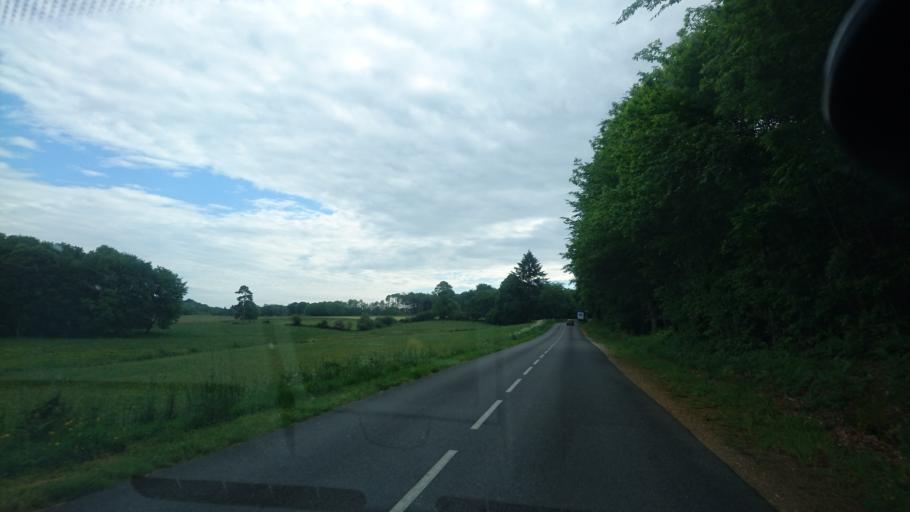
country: FR
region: Limousin
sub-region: Departement de la Haute-Vienne
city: Chateauneuf-la-Foret
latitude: 45.6805
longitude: 1.5753
